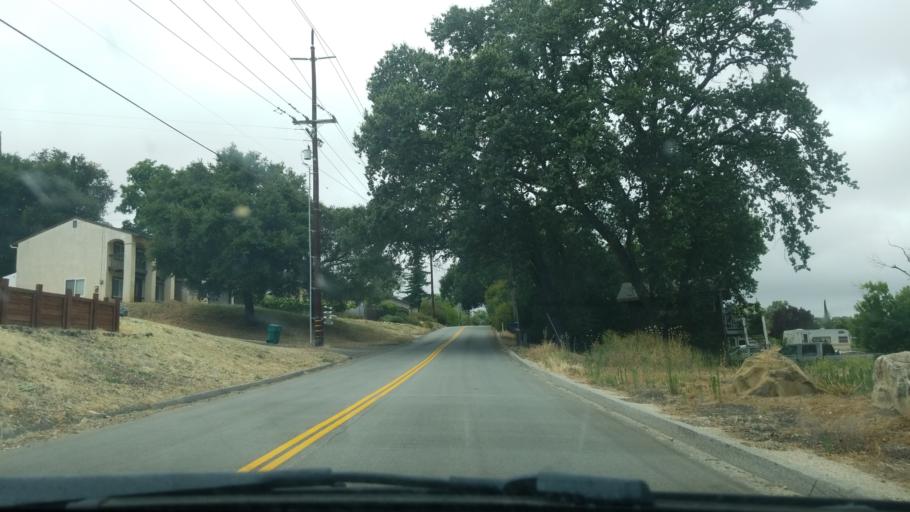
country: US
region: California
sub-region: San Luis Obispo County
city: Atascadero
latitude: 35.4622
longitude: -120.6662
